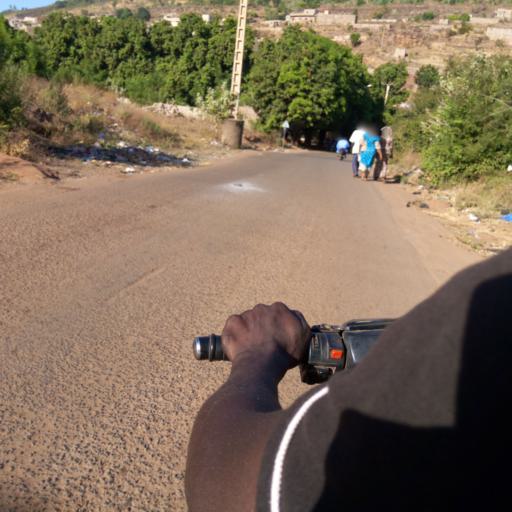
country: ML
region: Bamako
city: Bamako
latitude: 12.6599
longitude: -8.0356
